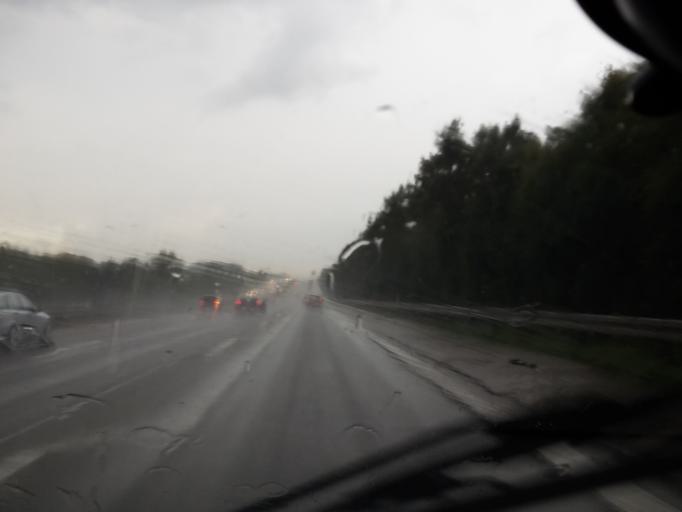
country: DE
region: Hesse
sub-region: Regierungsbezirk Darmstadt
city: Niedernhausen
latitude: 50.1056
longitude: 8.3471
